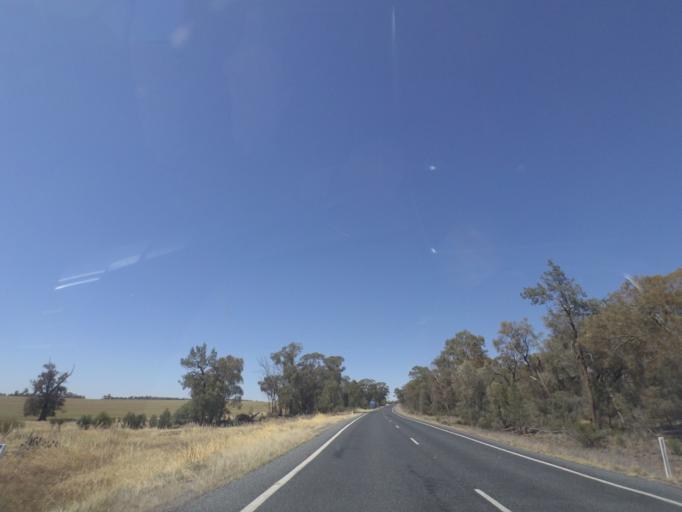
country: AU
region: New South Wales
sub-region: Narrandera
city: Narrandera
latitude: -34.4406
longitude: 146.8414
